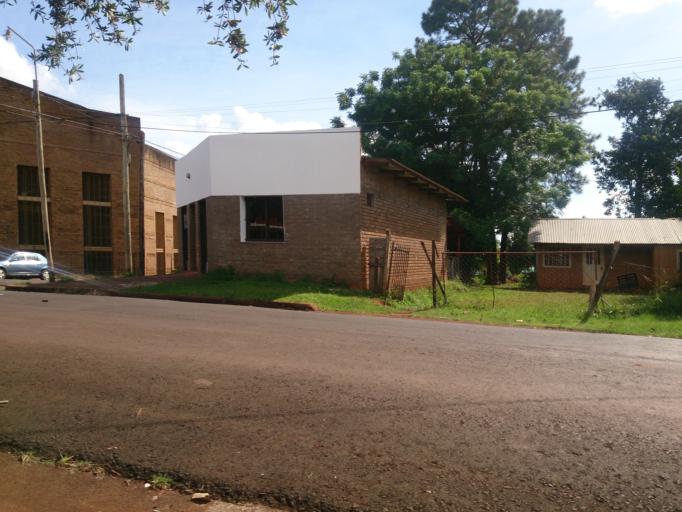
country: AR
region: Misiones
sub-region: Departamento de Obera
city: Obera
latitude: -27.4934
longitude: -55.1237
